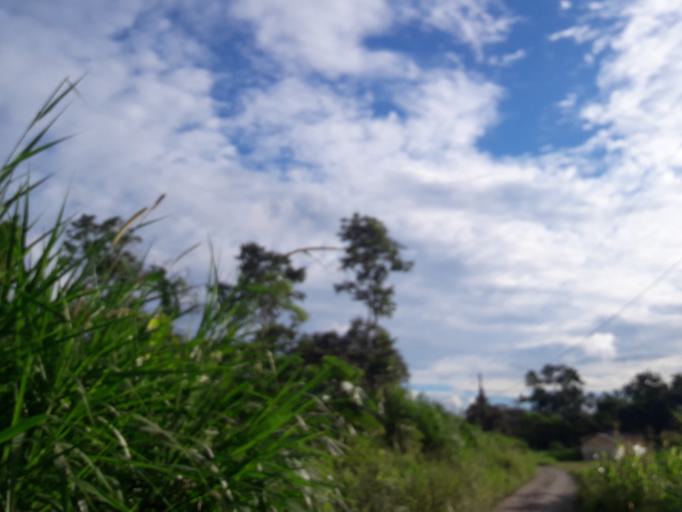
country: EC
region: Orellana
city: Boca Suno
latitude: -0.8876
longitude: -77.3012
